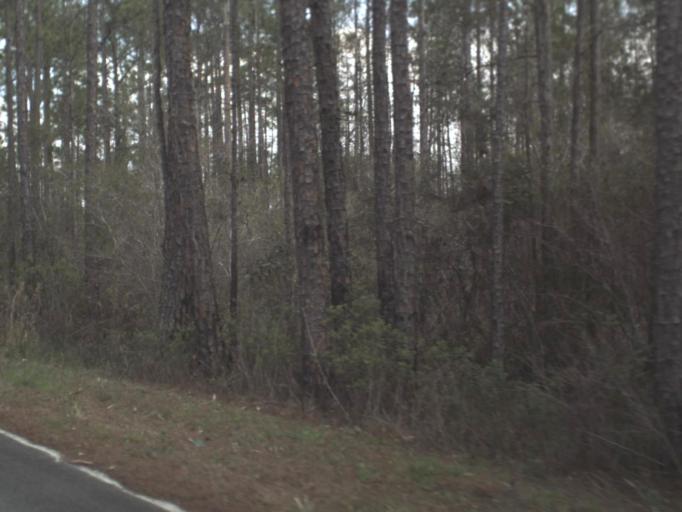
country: US
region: Florida
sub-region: Franklin County
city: Apalachicola
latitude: 29.9619
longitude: -84.9760
